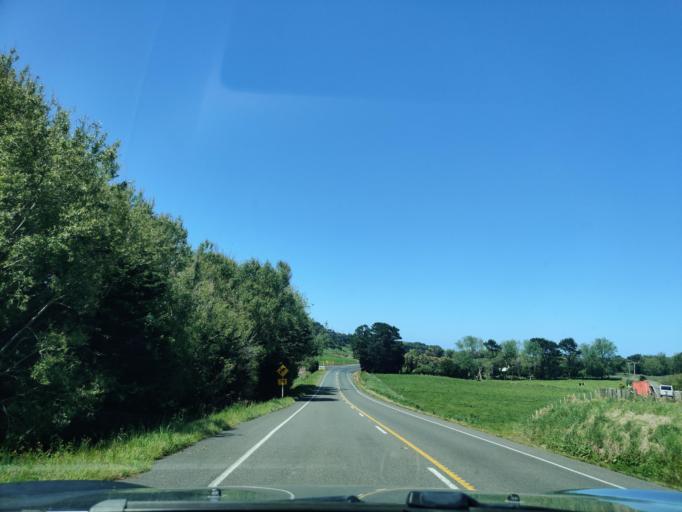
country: NZ
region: Taranaki
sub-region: South Taranaki District
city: Patea
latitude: -39.7525
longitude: 174.4858
